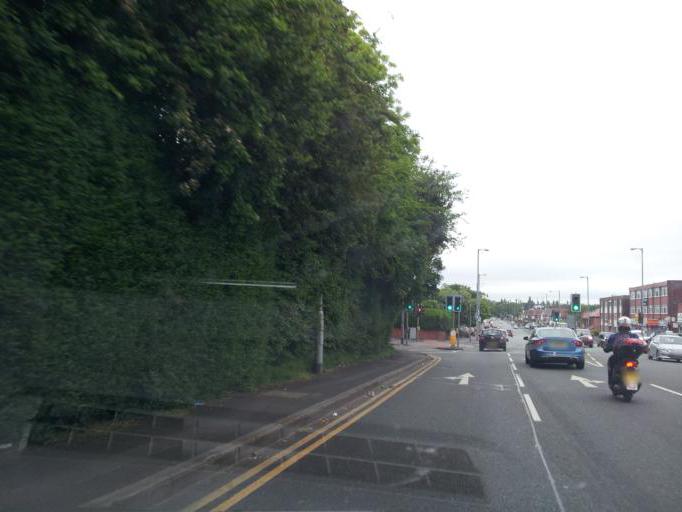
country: GB
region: England
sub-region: Manchester
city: Crumpsall
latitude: 53.5253
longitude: -2.2484
